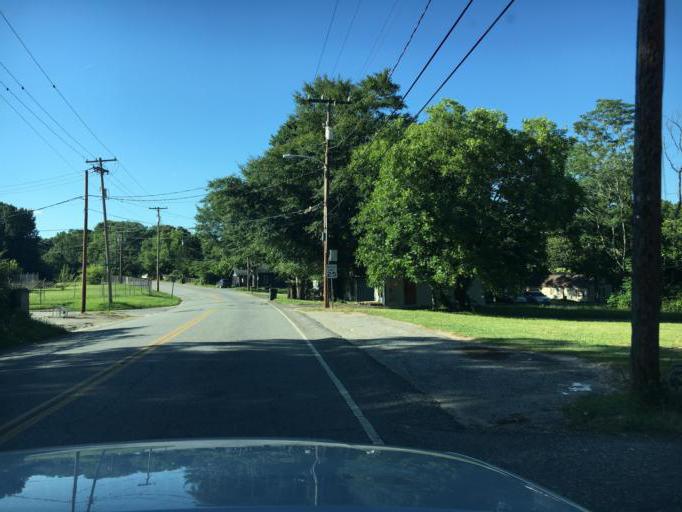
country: US
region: South Carolina
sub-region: Greenville County
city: Greer
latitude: 34.9410
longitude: -82.2156
